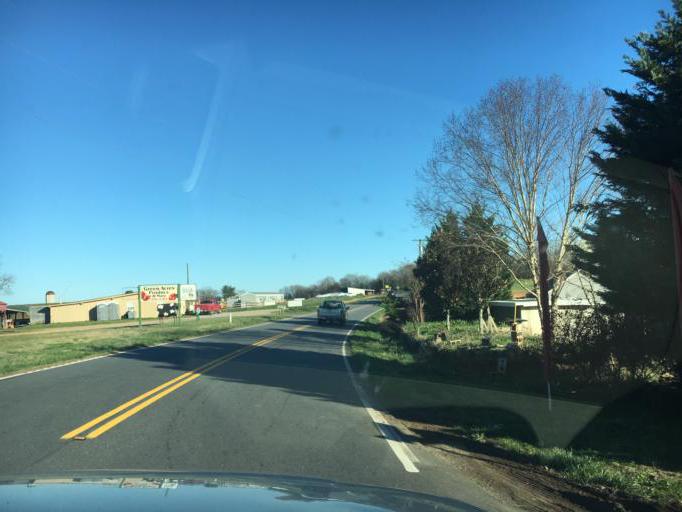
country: US
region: South Carolina
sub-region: Spartanburg County
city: Roebuck
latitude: 34.8804
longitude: -82.0193
